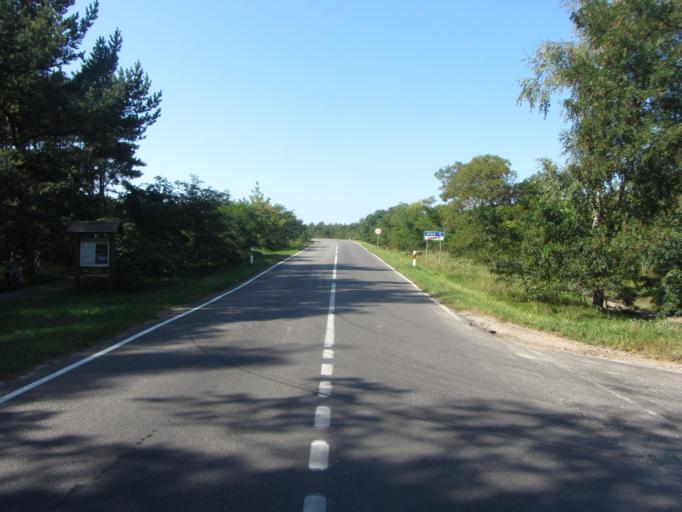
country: LT
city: Neringa
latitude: 55.3731
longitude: 21.0635
